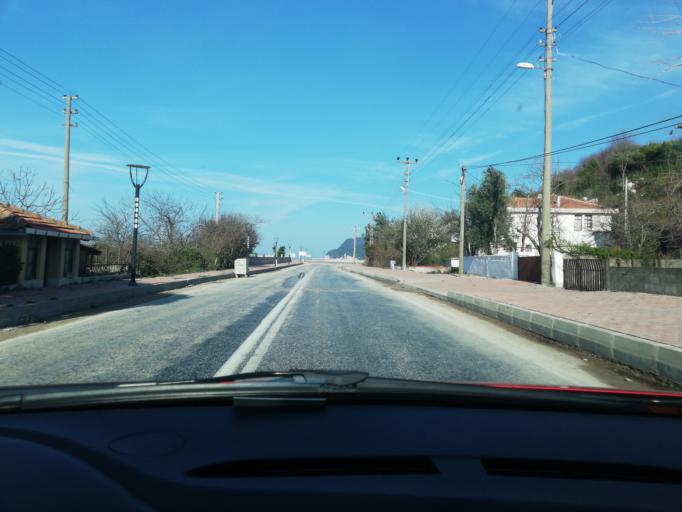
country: TR
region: Kastamonu
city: Cide
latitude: 41.8820
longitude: 32.9452
